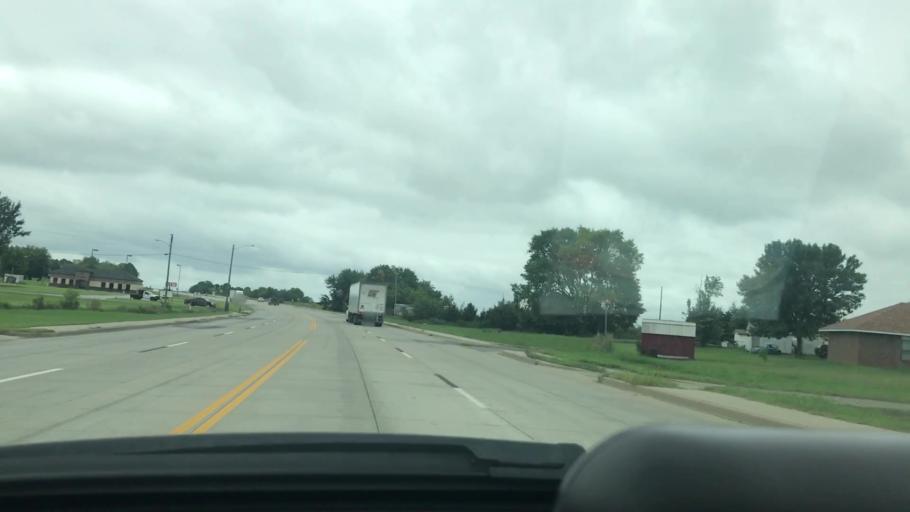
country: US
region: Oklahoma
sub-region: Pittsburg County
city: McAlester
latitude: 34.7253
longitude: -95.8983
